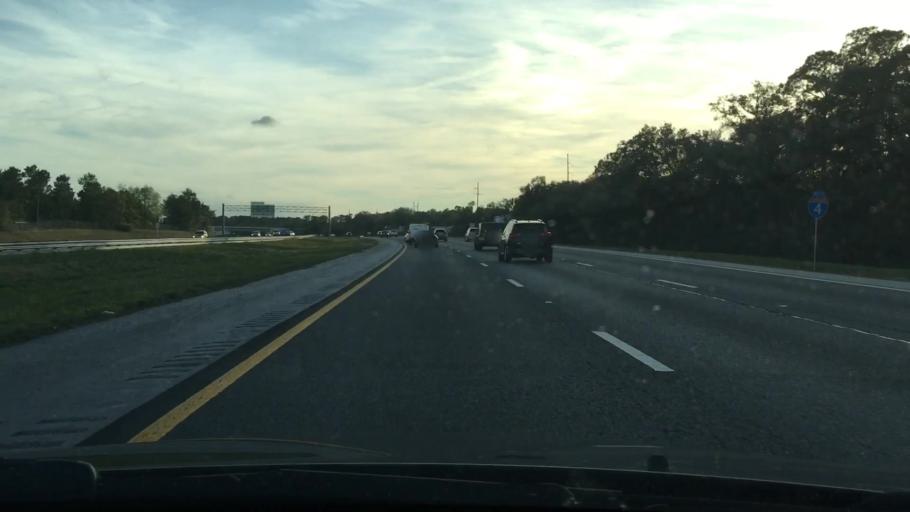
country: US
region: Florida
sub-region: Volusia County
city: Lake Helen
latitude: 29.0109
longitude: -81.2394
